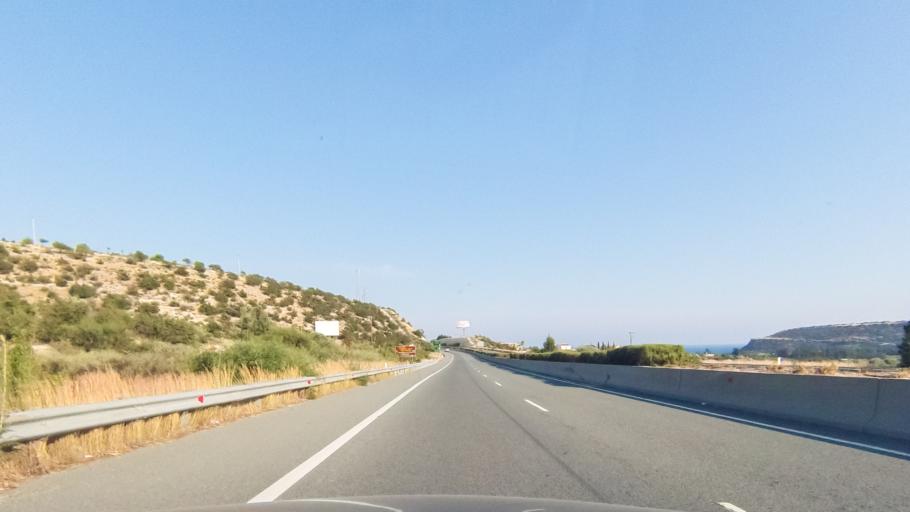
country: CY
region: Limassol
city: Sotira
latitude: 34.6828
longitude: 32.7908
